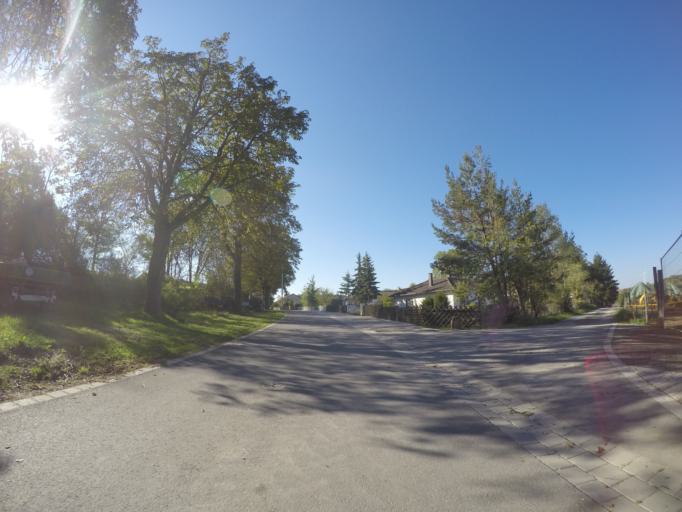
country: DE
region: Bavaria
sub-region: Regierungsbezirk Unterfranken
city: Remlingen
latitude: 49.8089
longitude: 9.6944
